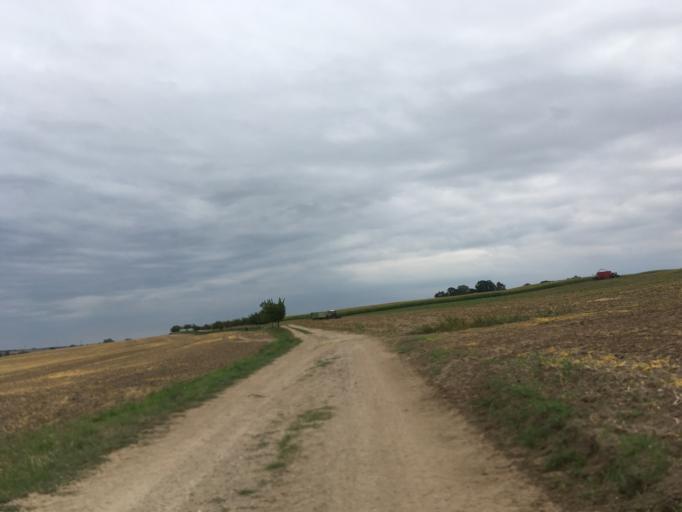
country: DE
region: Brandenburg
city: Angermunde
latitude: 53.0699
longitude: 14.0089
